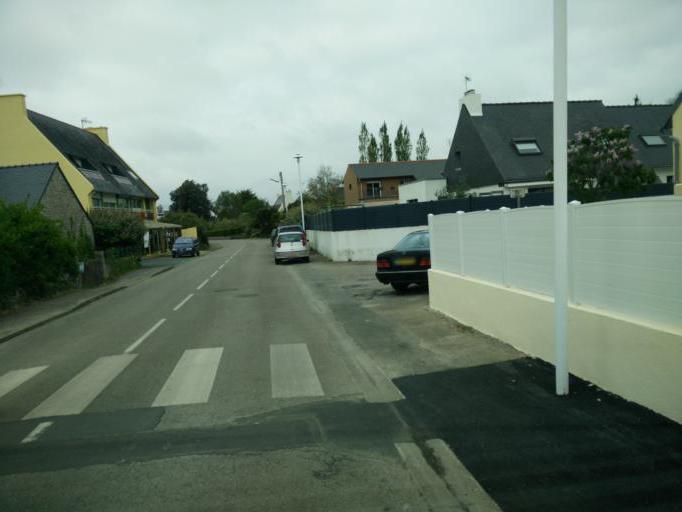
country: FR
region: Brittany
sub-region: Departement du Finistere
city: Loctudy
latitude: 47.8230
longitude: -4.1637
